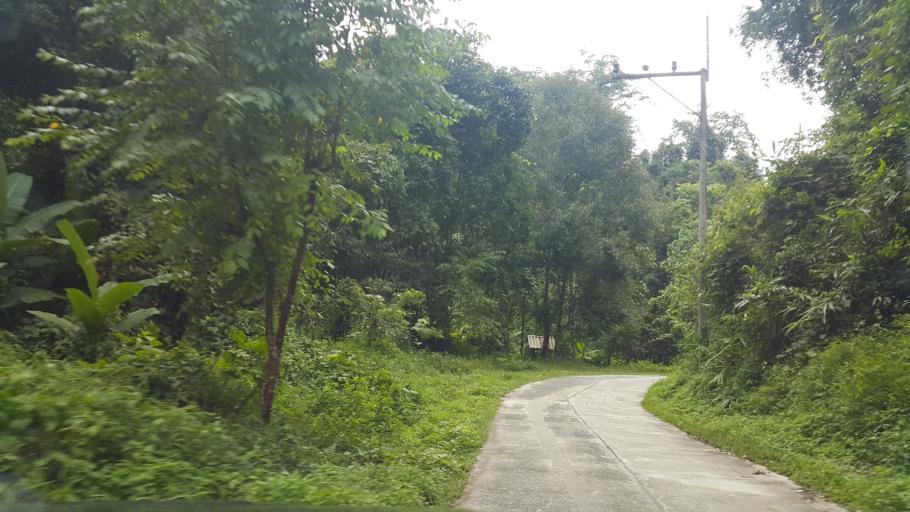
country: TH
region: Lampang
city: Wang Nuea
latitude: 19.0804
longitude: 99.3857
